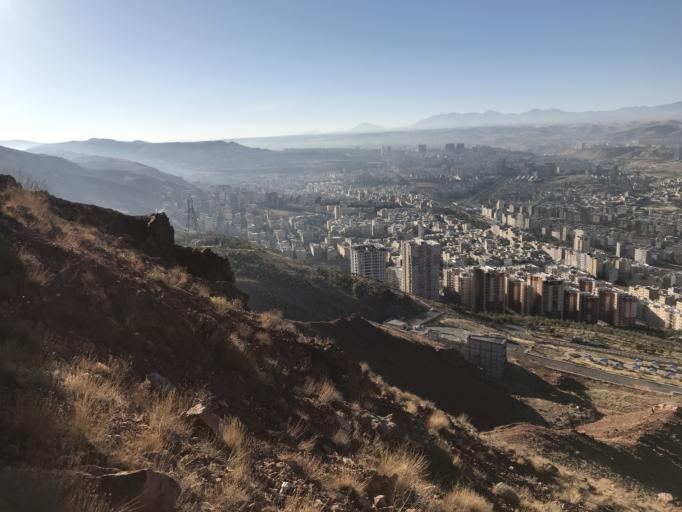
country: IR
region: East Azerbaijan
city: Tabriz
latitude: 38.0847
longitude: 46.3741
